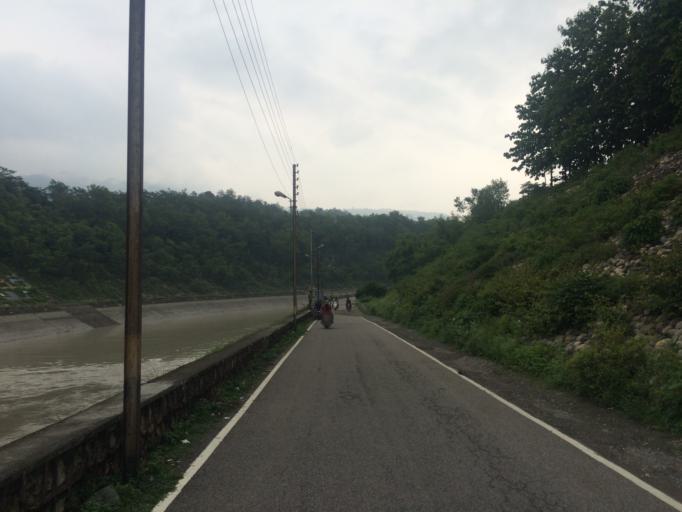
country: IN
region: Uttarakhand
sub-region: Dehradun
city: Birbhaddar
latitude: 30.0731
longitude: 78.2907
